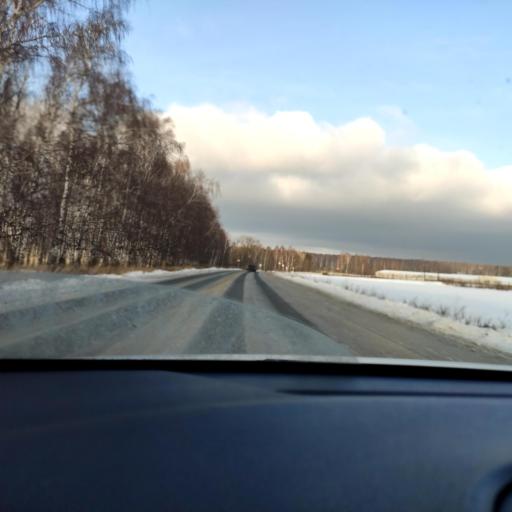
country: RU
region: Tatarstan
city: Osinovo
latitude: 55.8926
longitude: 48.8900
